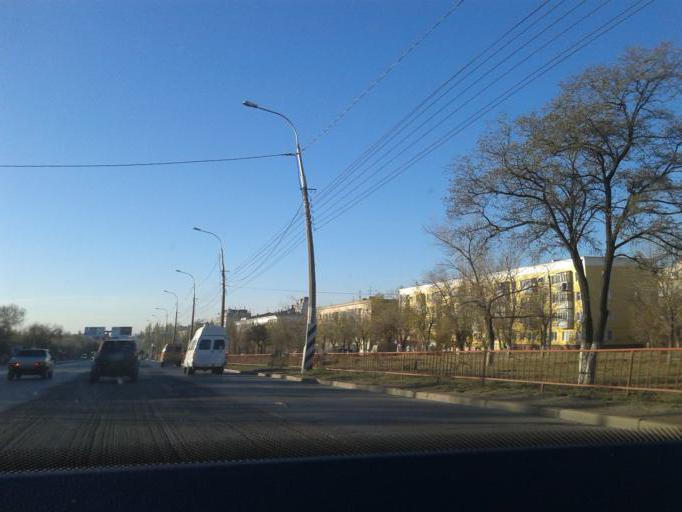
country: RU
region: Volgograd
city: Volgograd
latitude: 48.6612
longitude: 44.4389
